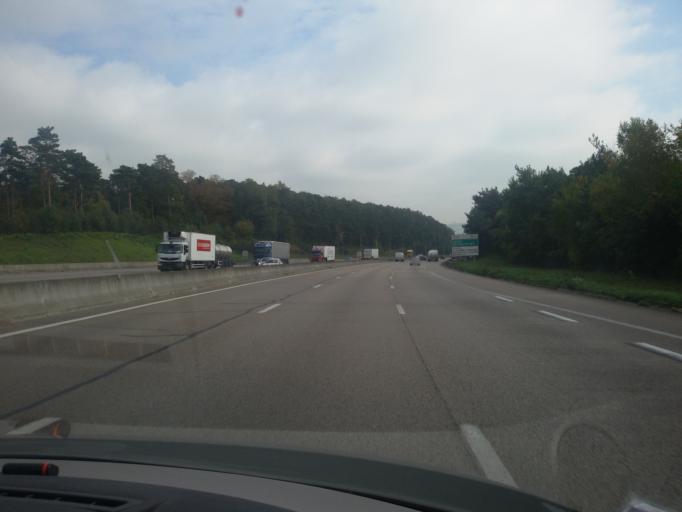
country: FR
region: Haute-Normandie
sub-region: Departement de la Seine-Maritime
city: Oissel
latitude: 49.3424
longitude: 1.0629
